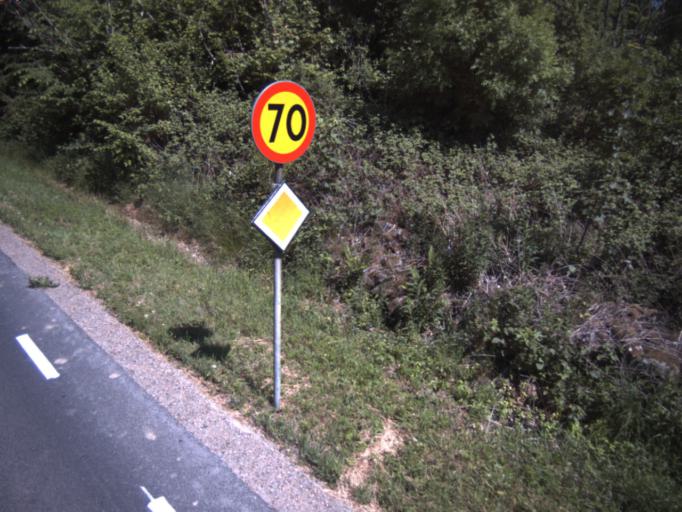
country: DK
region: Capital Region
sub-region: Helsingor Kommune
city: Helsingor
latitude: 56.1076
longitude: 12.6387
